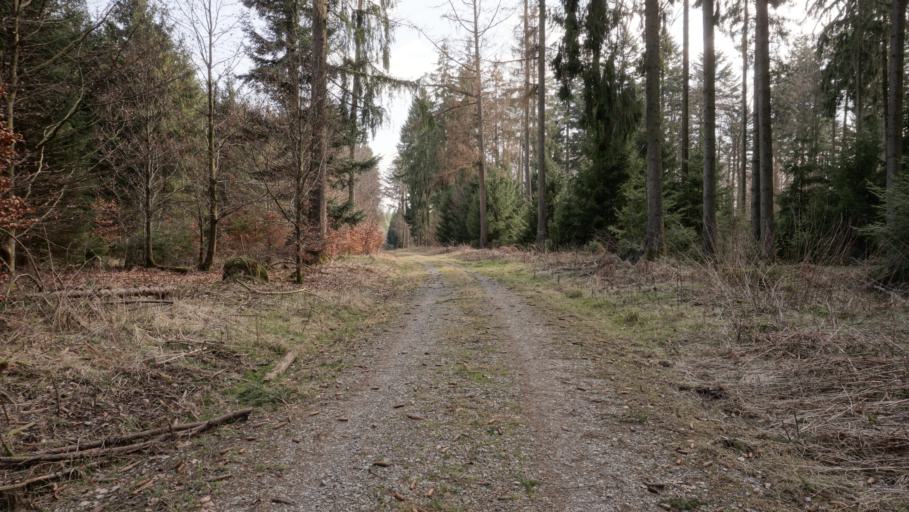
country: DE
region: Baden-Wuerttemberg
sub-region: Karlsruhe Region
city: Fahrenbach
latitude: 49.4484
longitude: 9.1327
